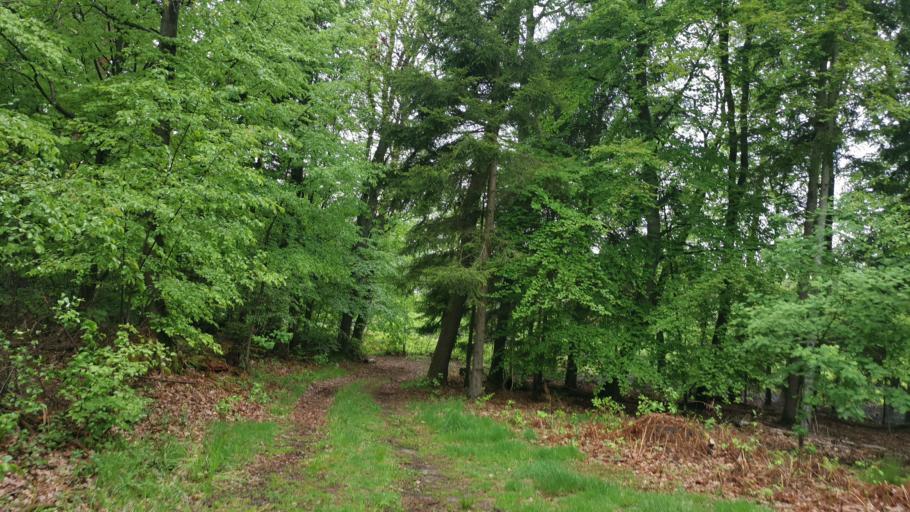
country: DE
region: Saarland
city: Kirkel
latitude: 49.2739
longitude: 7.1840
